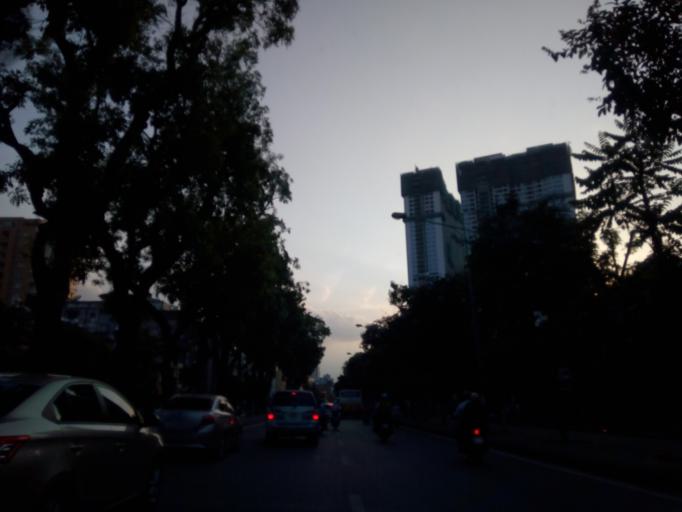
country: VN
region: Ha Noi
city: Dong Da
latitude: 21.0307
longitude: 105.8190
